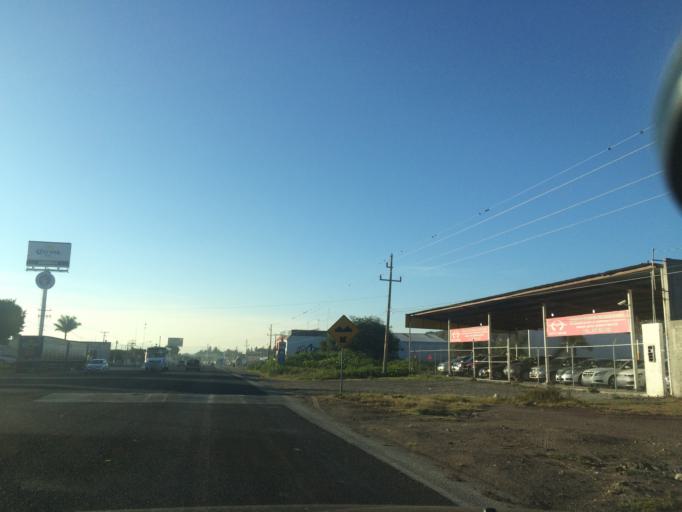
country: MX
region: Puebla
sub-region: Santiago Miahuatlan
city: San Jose Monte Chiquito
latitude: 18.4793
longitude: -97.4428
